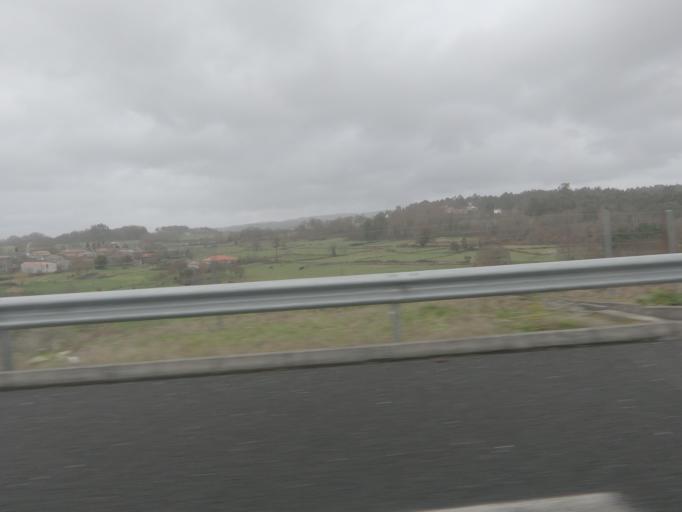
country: ES
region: Galicia
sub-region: Provincia de Pontevedra
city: Silleda
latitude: 42.6928
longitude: -8.1947
